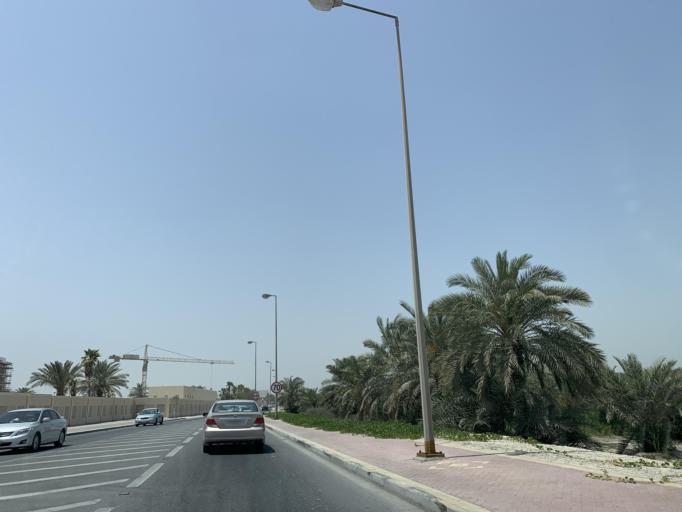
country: BH
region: Manama
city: Jidd Hafs
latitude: 26.1969
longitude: 50.5549
